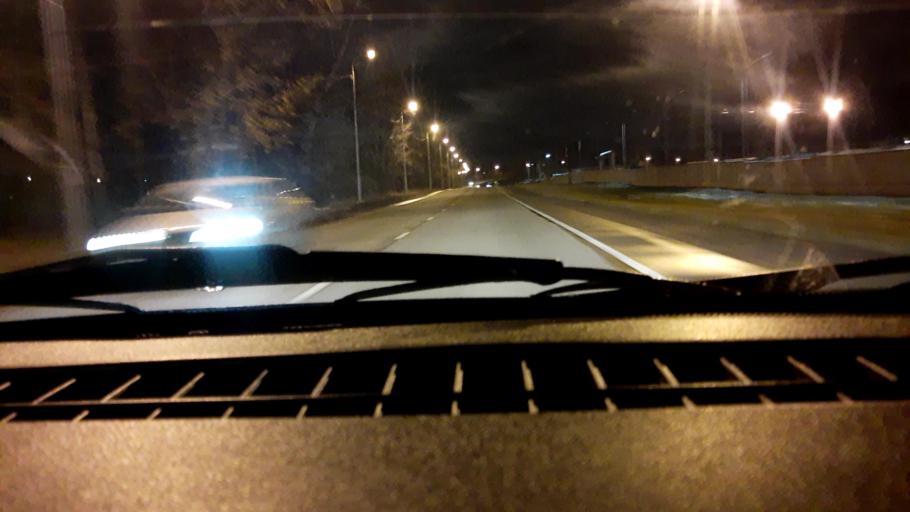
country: RU
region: Bashkortostan
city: Blagoveshchensk
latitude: 54.9142
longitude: 56.0655
